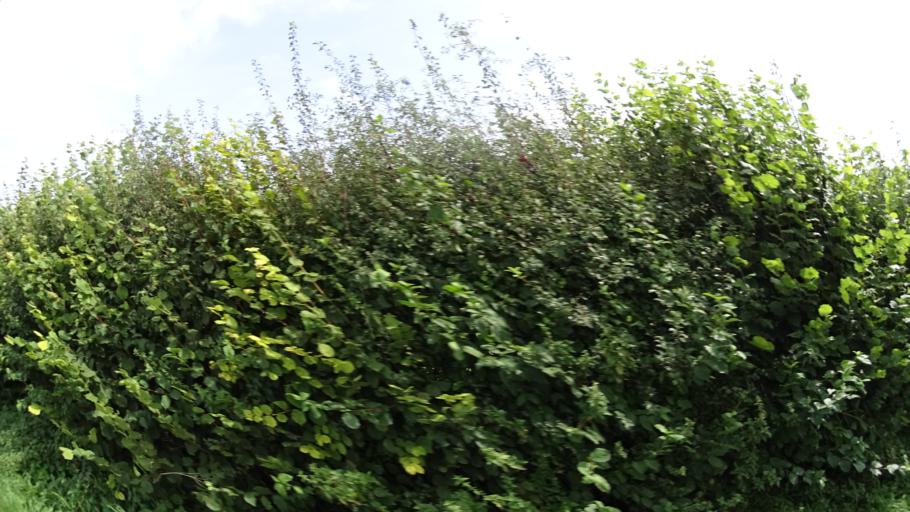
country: GB
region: England
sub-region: Dorset
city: Wimborne Minster
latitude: 50.8961
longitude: -2.0333
